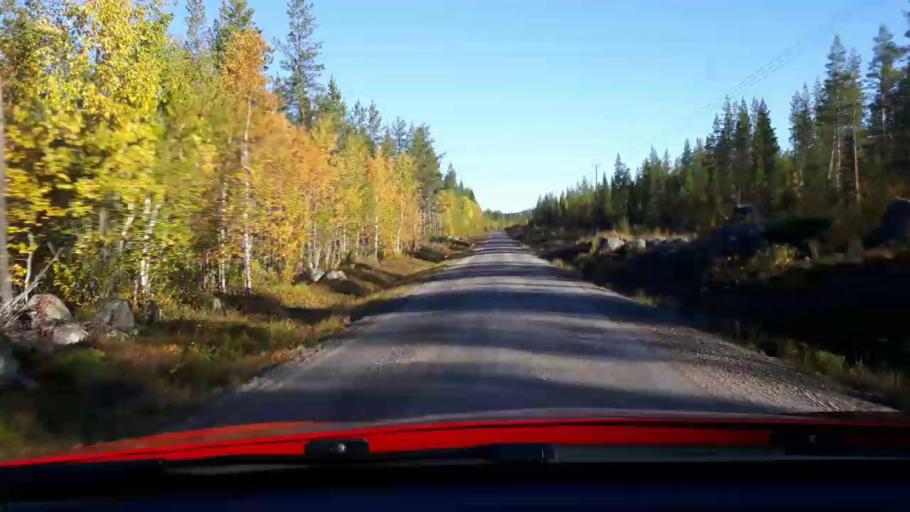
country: SE
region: Jaemtland
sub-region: Stroemsunds Kommun
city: Stroemsund
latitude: 64.3869
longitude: 15.1518
